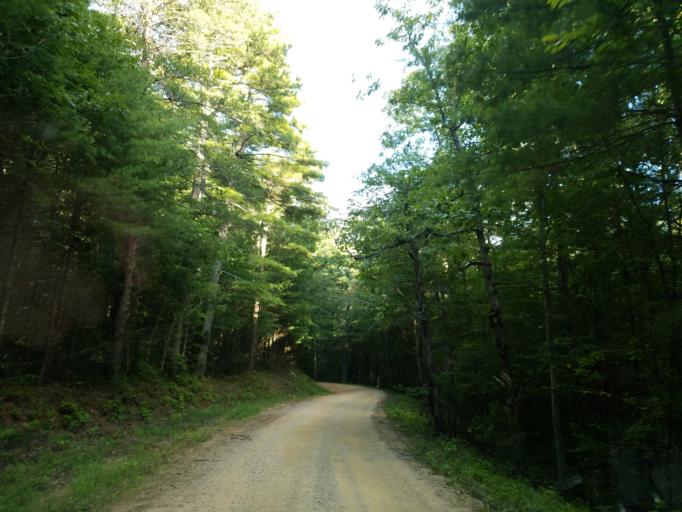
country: US
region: Georgia
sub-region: Union County
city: Blairsville
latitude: 34.7479
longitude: -84.0671
